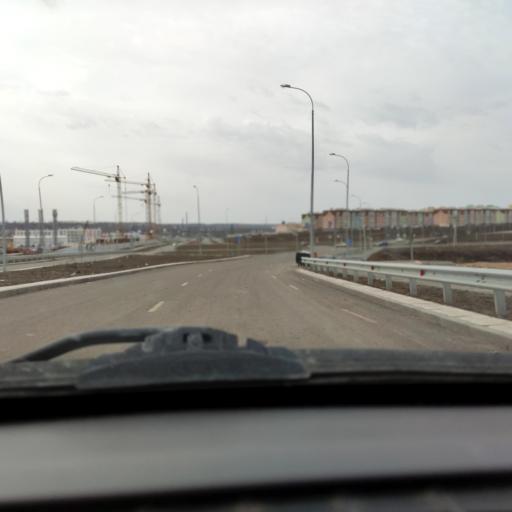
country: RU
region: Samara
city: Petra-Dubrava
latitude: 53.2932
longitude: 50.3305
